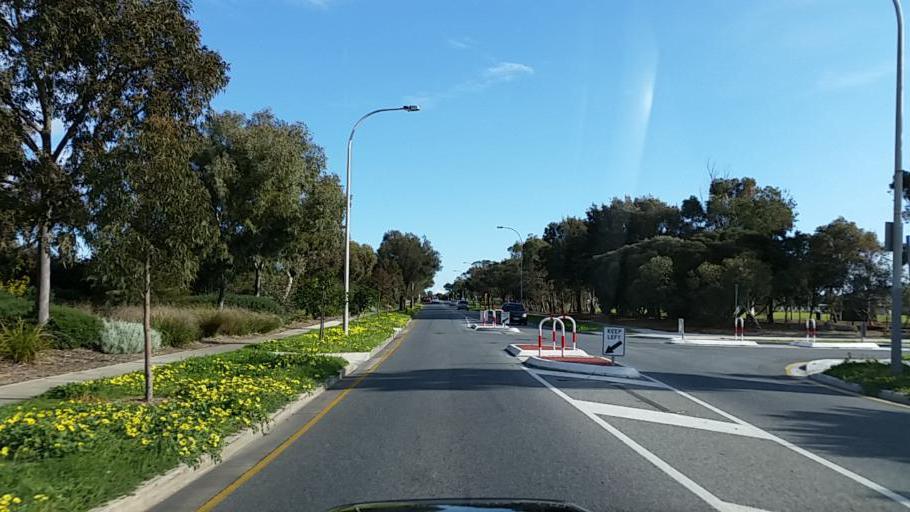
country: AU
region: South Australia
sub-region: Charles Sturt
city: West Lakes Shore
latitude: -34.8626
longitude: 138.4870
